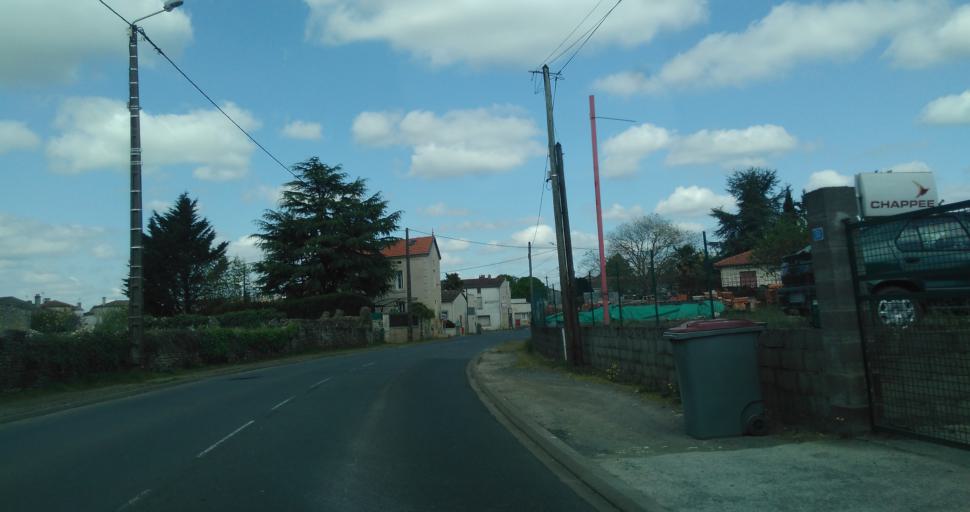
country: FR
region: Poitou-Charentes
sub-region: Departement des Deux-Sevres
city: Villiers-en-Plaine
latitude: 46.4067
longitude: -0.5351
